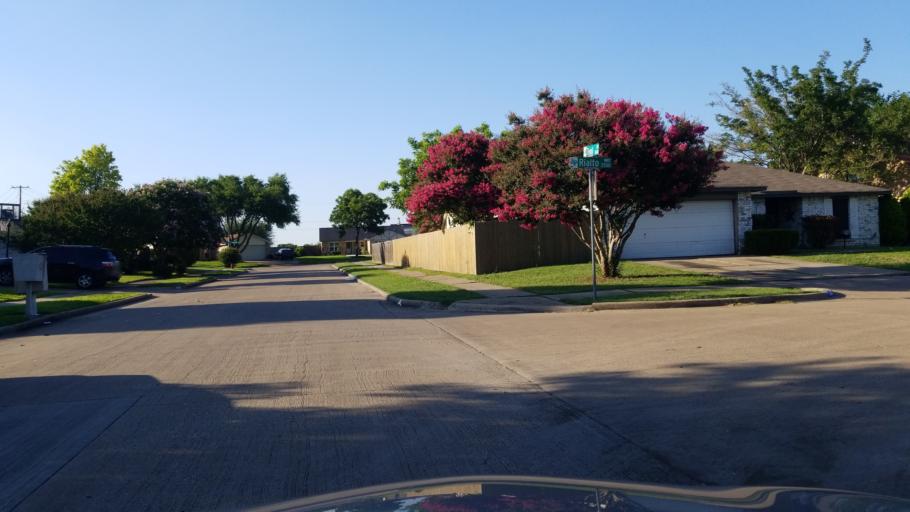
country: US
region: Texas
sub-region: Dallas County
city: Grand Prairie
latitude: 32.6826
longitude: -97.0437
